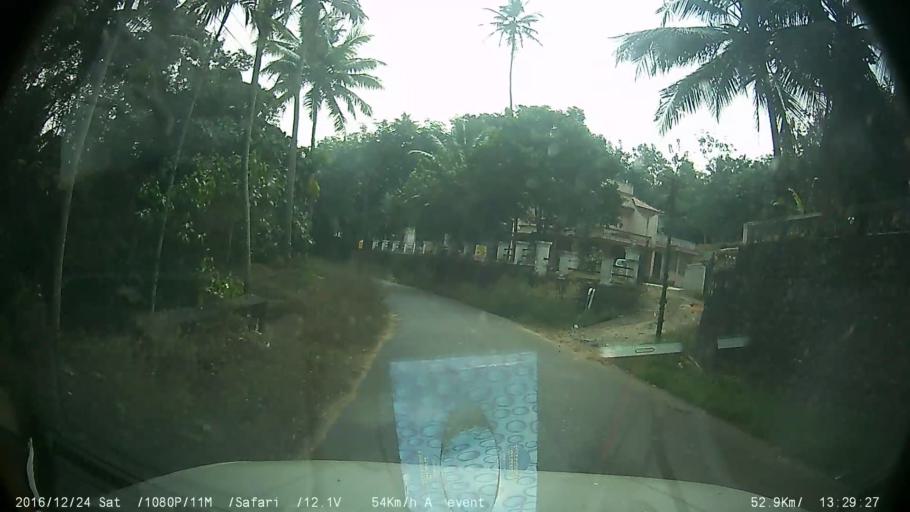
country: IN
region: Kerala
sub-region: Kottayam
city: Palackattumala
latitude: 9.8536
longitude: 76.6978
